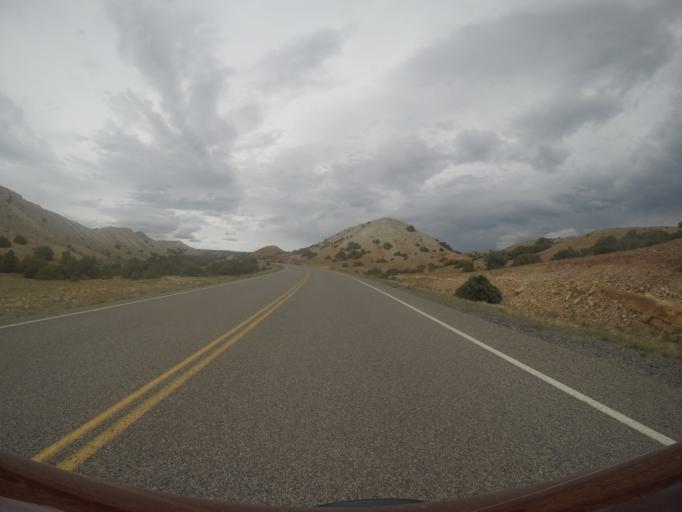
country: US
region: Wyoming
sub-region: Big Horn County
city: Lovell
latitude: 44.9722
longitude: -108.2632
